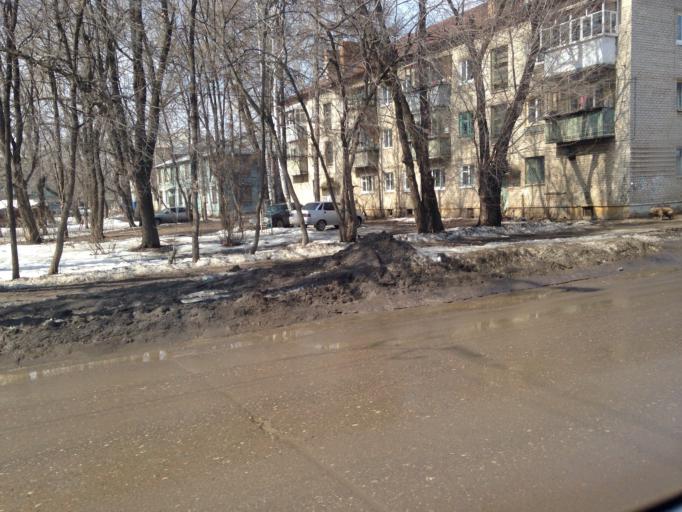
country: RU
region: Ulyanovsk
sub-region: Ulyanovskiy Rayon
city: Ulyanovsk
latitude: 54.3501
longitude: 48.5481
